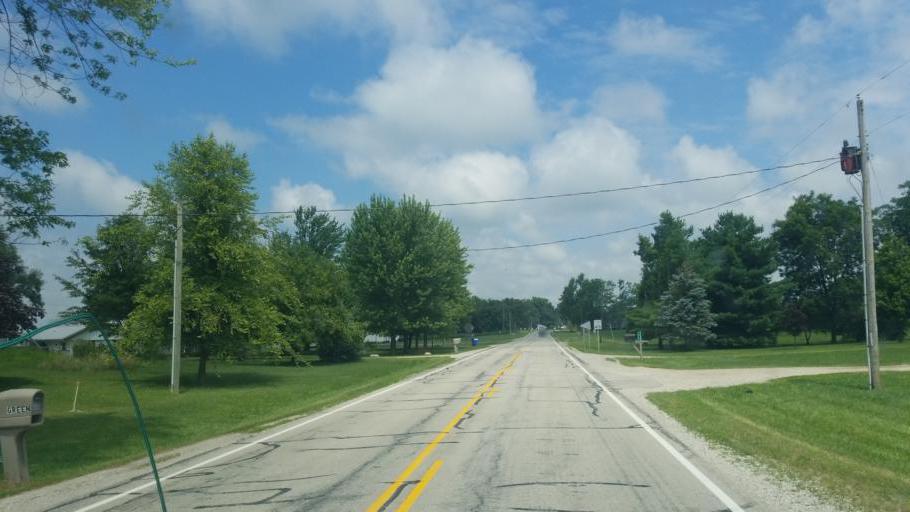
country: US
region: Indiana
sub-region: Huntington County
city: Warren
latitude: 40.6709
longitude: -85.4351
